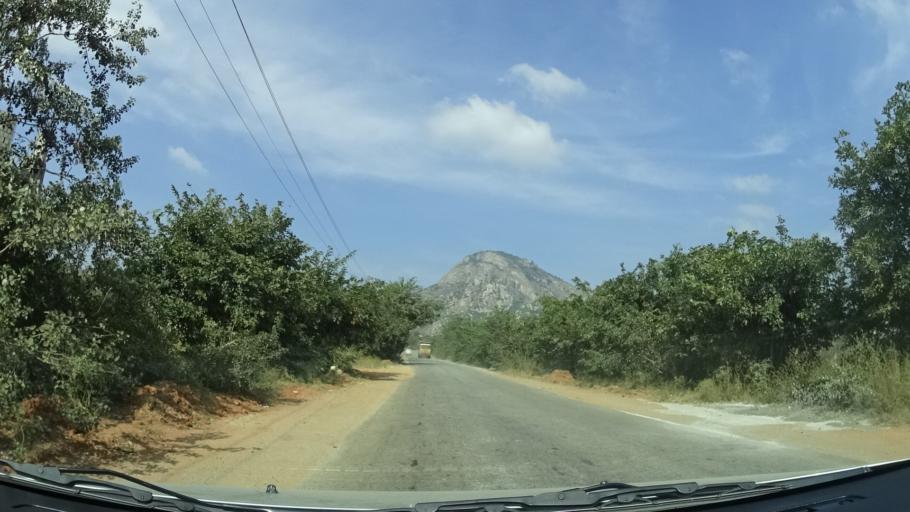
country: IN
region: Karnataka
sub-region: Chikkaballapur
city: Chik Ballapur
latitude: 13.4035
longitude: 77.7050
